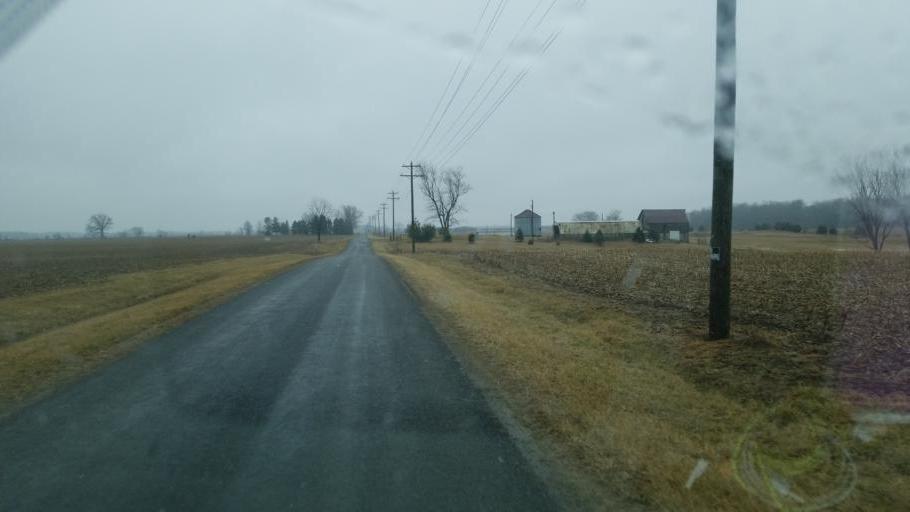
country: US
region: Ohio
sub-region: Union County
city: New California
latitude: 40.2054
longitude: -83.2678
